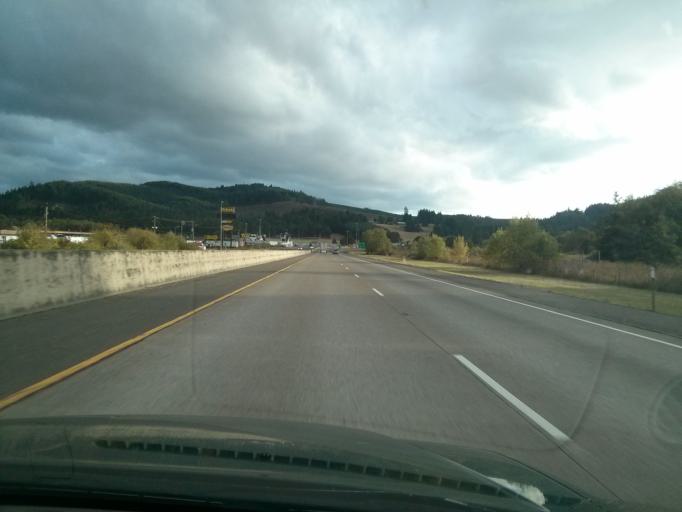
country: US
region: Oregon
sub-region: Douglas County
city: Yoncalla
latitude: 43.5425
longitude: -123.2898
